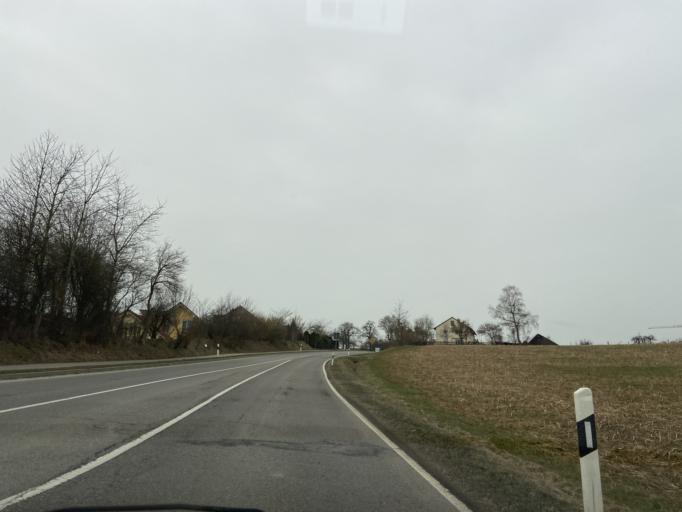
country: DE
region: Baden-Wuerttemberg
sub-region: Tuebingen Region
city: Illmensee
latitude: 47.8739
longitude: 9.3744
